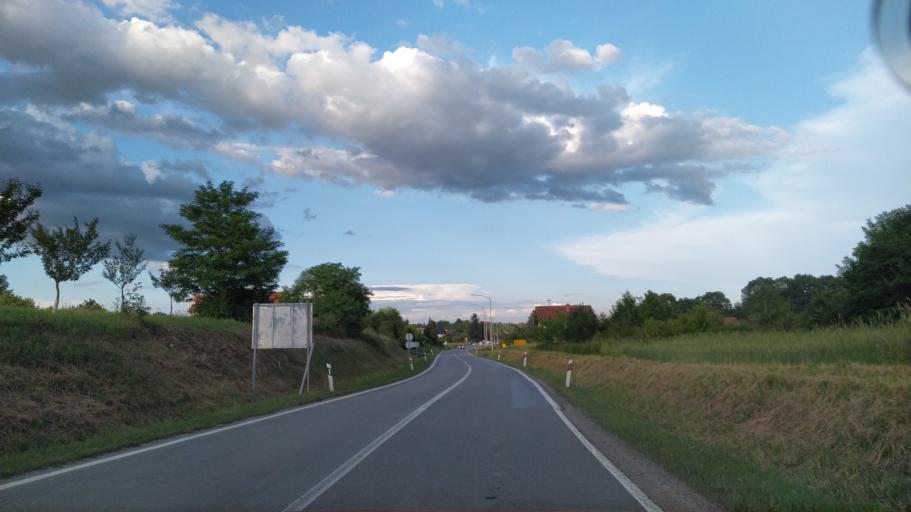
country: HR
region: Osjecko-Baranjska
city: Martin
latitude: 45.4915
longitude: 18.0565
